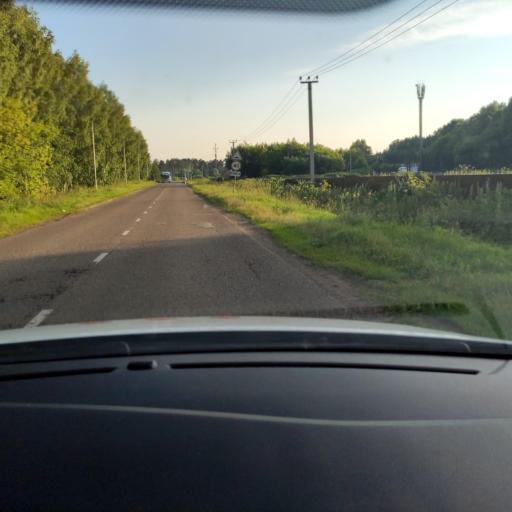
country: RU
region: Tatarstan
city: Vysokaya Gora
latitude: 55.9723
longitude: 49.3049
